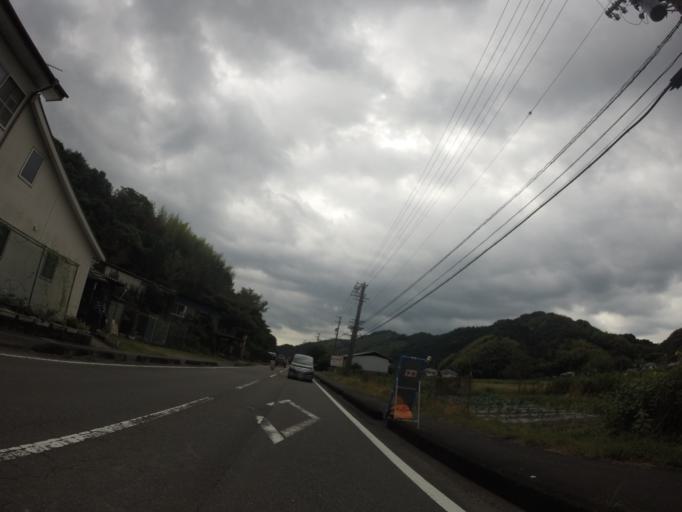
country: JP
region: Shizuoka
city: Fujieda
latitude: 34.9066
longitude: 138.2620
